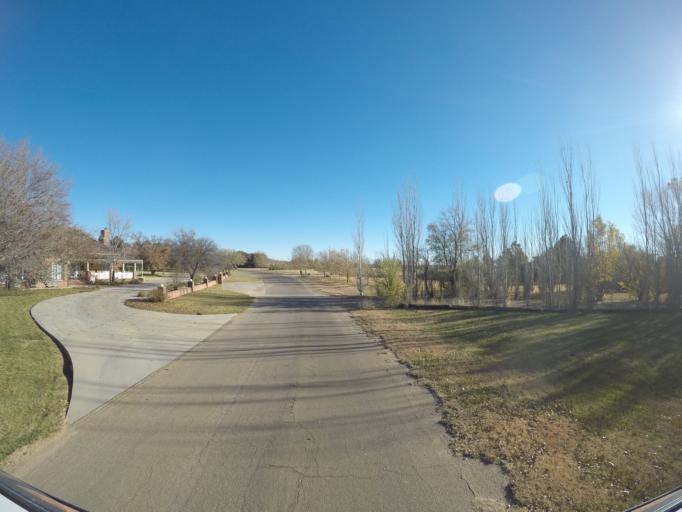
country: US
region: New Mexico
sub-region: Curry County
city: Clovis
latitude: 34.4277
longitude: -103.1688
